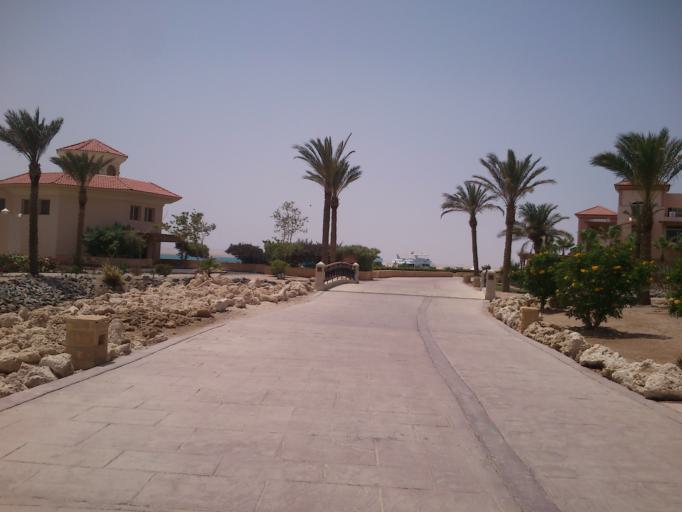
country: EG
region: Red Sea
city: Bur Safajah
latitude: 26.8478
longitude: 33.9859
